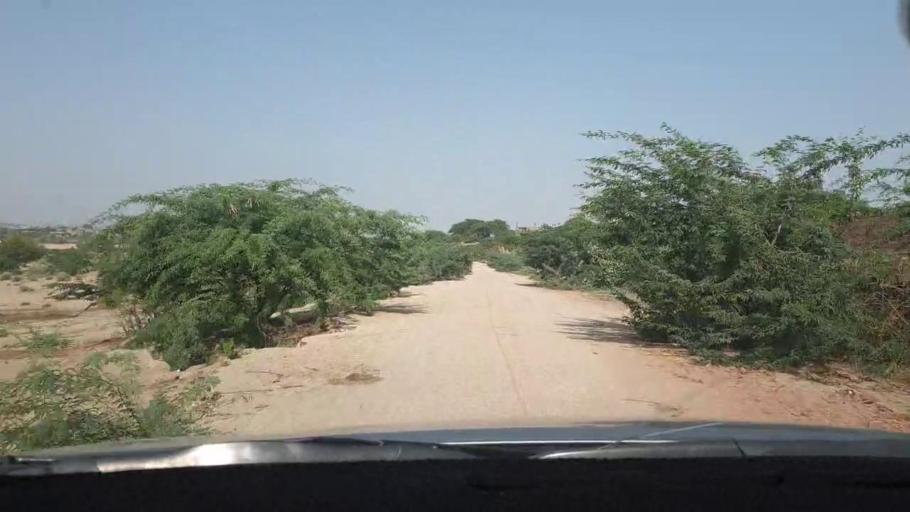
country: PK
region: Sindh
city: Pithoro
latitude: 25.7777
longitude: 69.4732
